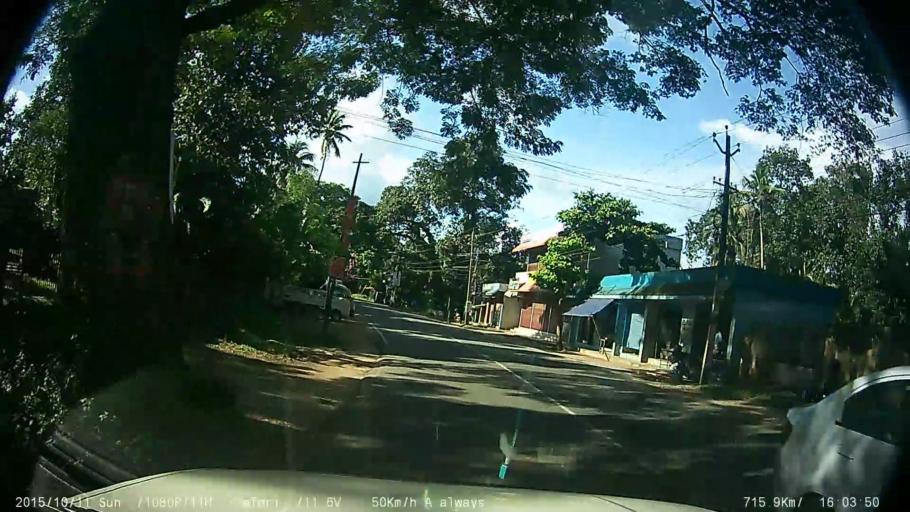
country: IN
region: Kerala
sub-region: Kottayam
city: Palackattumala
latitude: 9.6732
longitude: 76.6107
